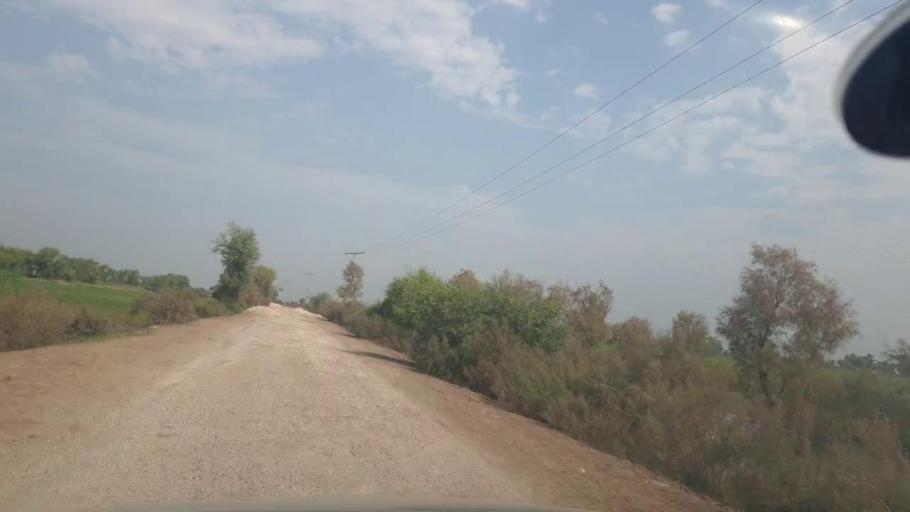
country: PK
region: Balochistan
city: Mehrabpur
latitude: 28.0656
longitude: 68.1036
